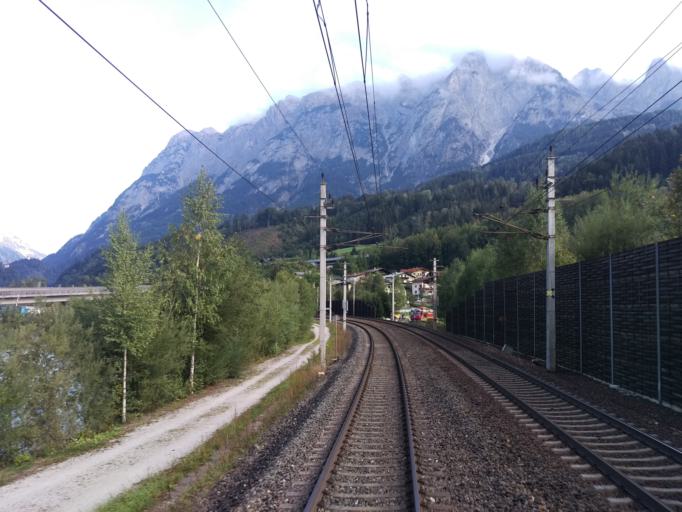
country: AT
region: Salzburg
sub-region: Politischer Bezirk Sankt Johann im Pongau
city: Pfarrwerfen
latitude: 47.4644
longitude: 13.2000
